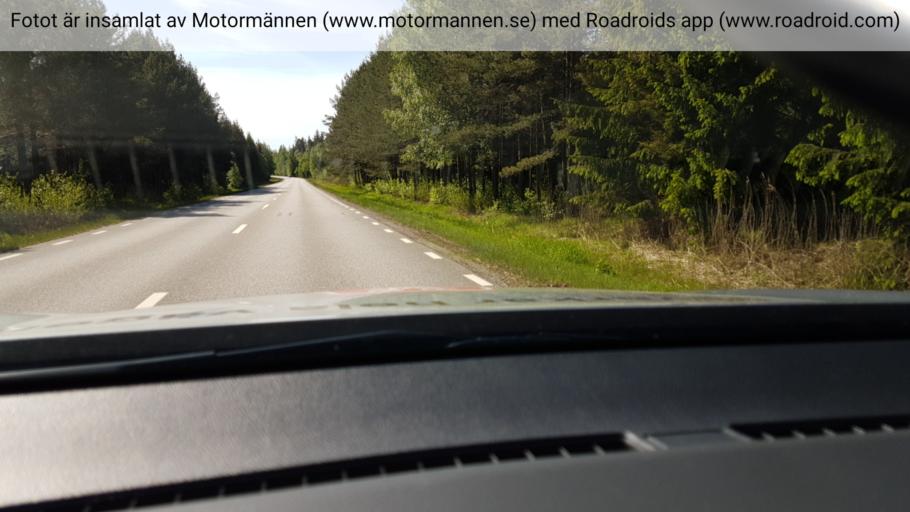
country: SE
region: Vaestra Goetaland
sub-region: Tibro Kommun
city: Tibro
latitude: 58.3712
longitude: 14.2056
